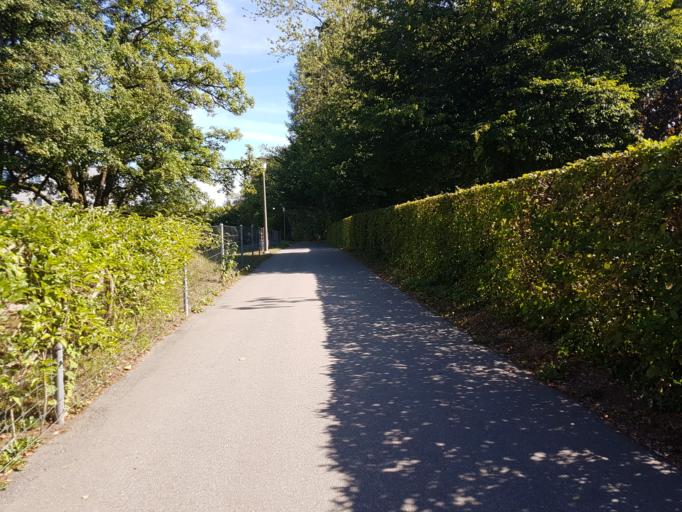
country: CH
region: Zurich
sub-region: Bezirk Pfaeffikon
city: Effretikon / Rappenhalde-Bannhalde
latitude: 47.4251
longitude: 8.6942
